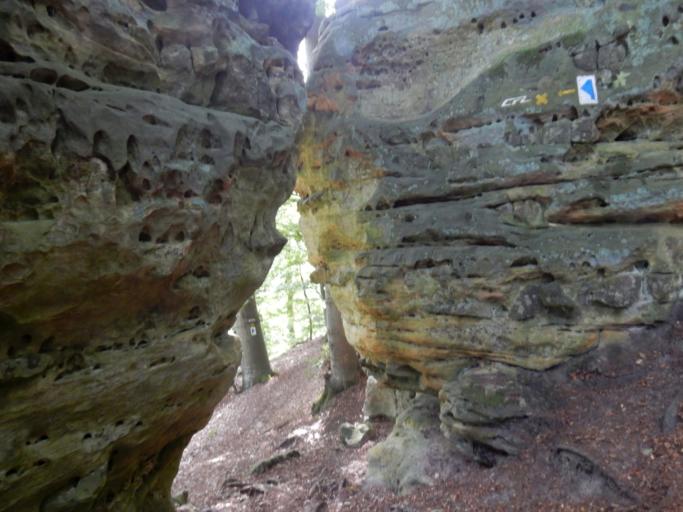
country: LU
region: Luxembourg
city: Rollingen
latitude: 49.7309
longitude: 6.0988
